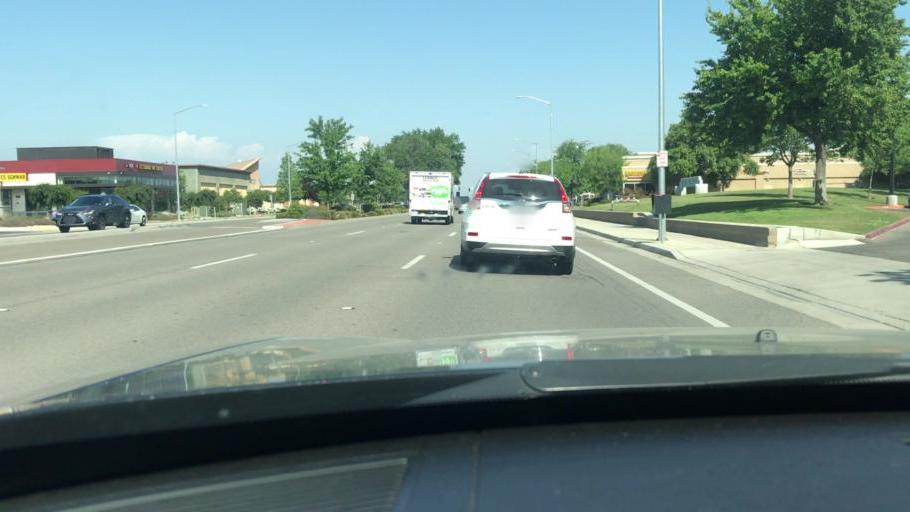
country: US
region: California
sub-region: Fresno County
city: Clovis
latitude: 36.8374
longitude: -119.6877
